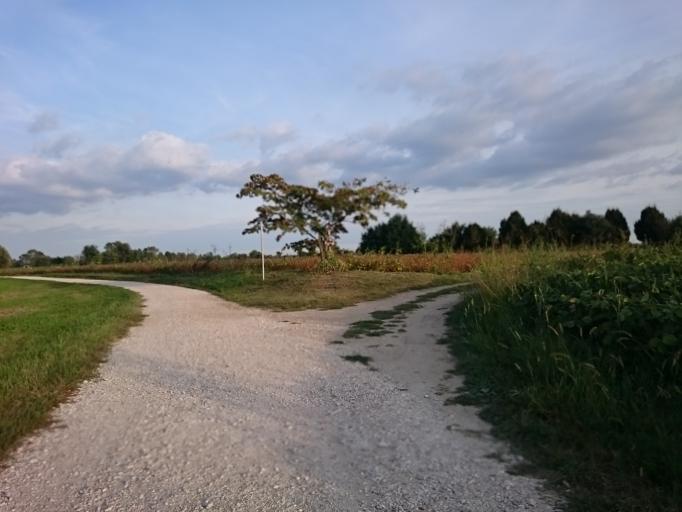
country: IT
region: Veneto
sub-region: Provincia di Vicenza
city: Camisano Vicentino
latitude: 45.5124
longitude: 11.7210
